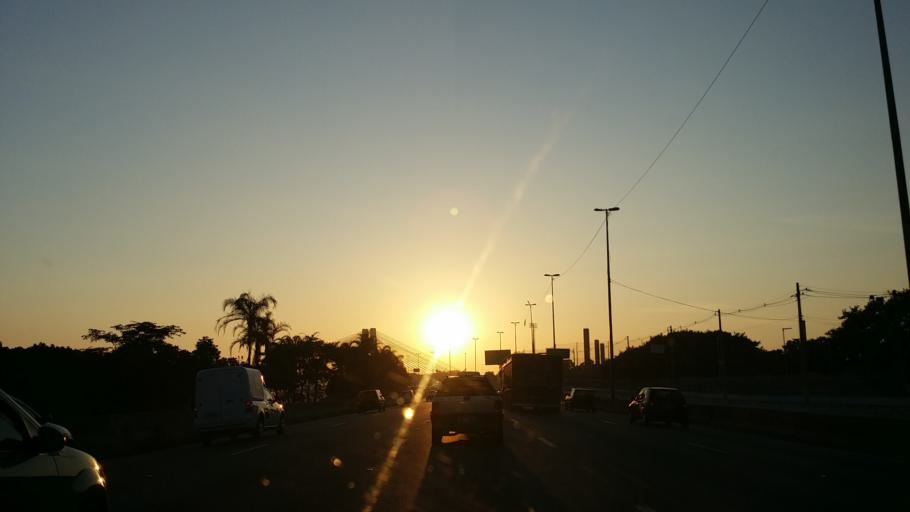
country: BR
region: Sao Paulo
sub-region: Sao Paulo
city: Sao Paulo
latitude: -23.5186
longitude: -46.6447
